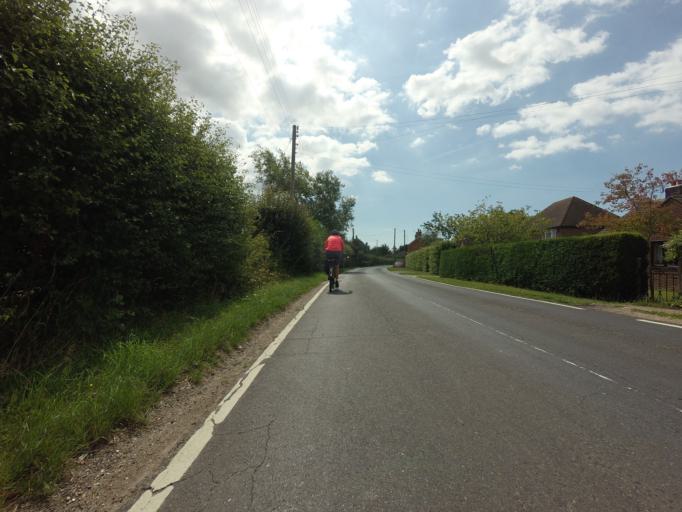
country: GB
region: England
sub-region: Kent
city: Stone
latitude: 51.0440
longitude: 0.7844
